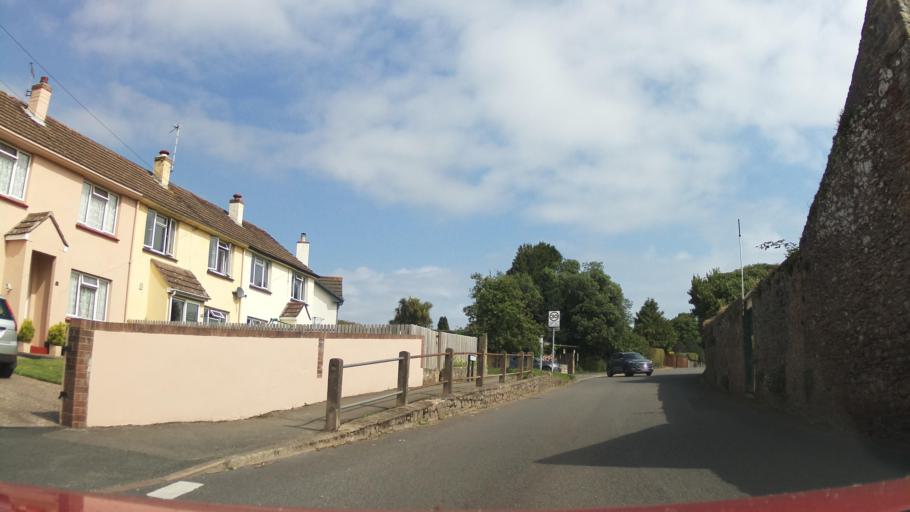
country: GB
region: England
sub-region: Devon
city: Marldon
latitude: 50.4072
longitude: -3.6237
